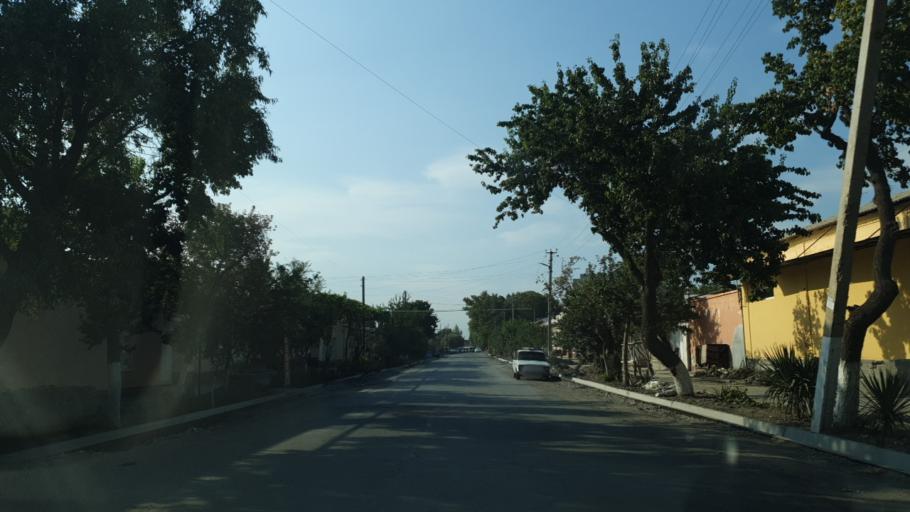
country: UZ
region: Fergana
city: Yaypan
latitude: 40.3765
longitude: 70.8119
